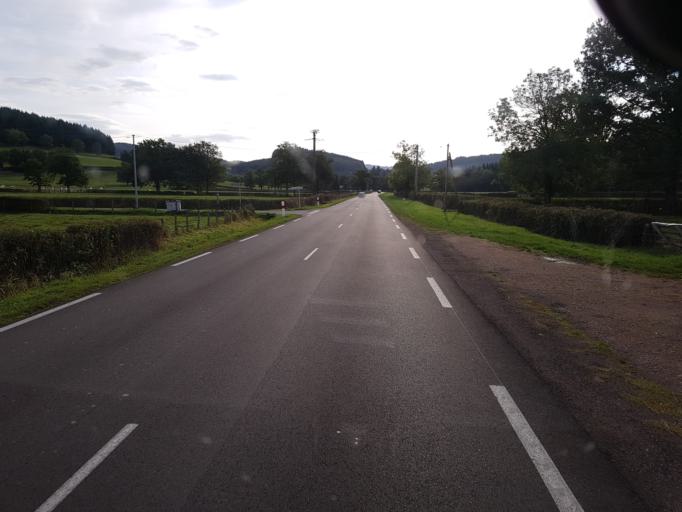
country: FR
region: Bourgogne
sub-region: Departement de Saone-et-Loire
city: La Clayette
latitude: 46.2821
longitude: 4.3586
